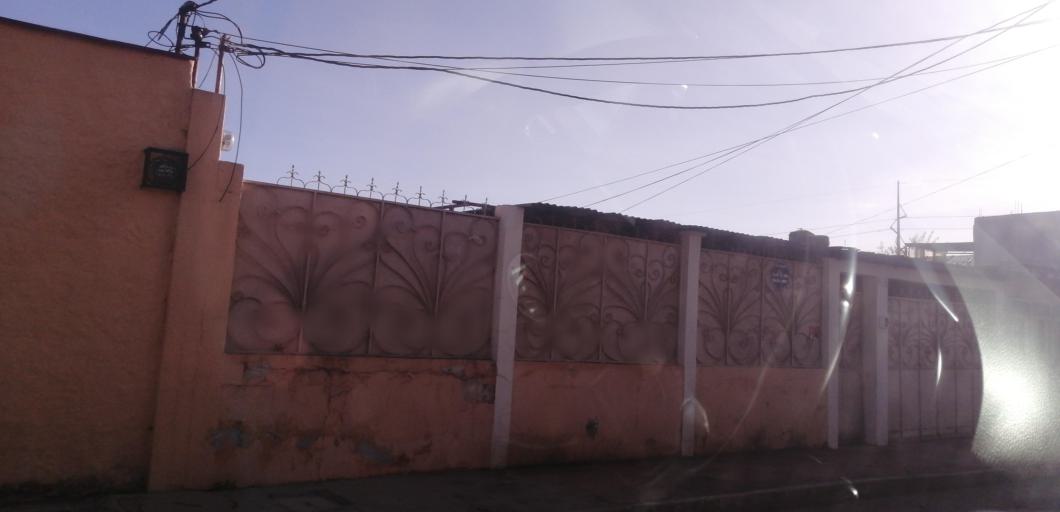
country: GT
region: Quetzaltenango
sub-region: Municipio de La Esperanza
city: La Esperanza
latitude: 14.8672
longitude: -91.5458
